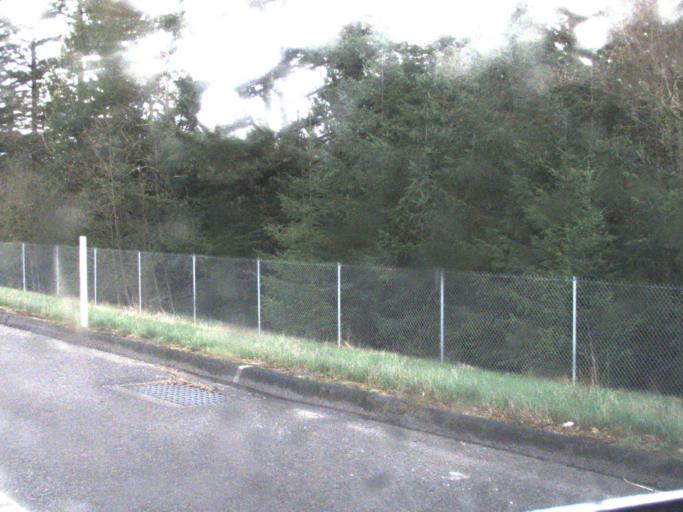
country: US
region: Washington
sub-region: King County
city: Maple Valley
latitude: 47.4120
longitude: -122.0251
